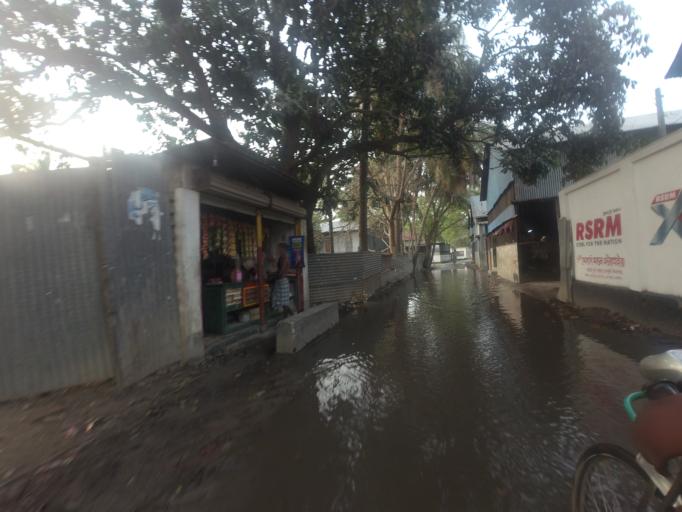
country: BD
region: Rajshahi
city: Sirajganj
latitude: 24.3300
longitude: 89.6916
